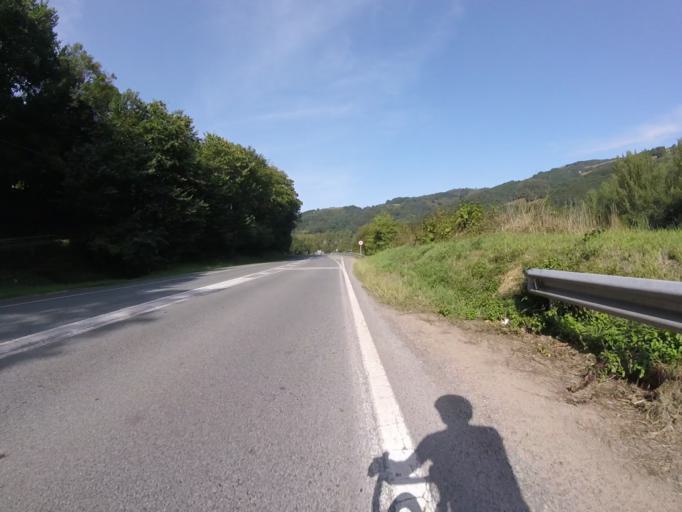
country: ES
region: Navarre
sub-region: Provincia de Navarra
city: Doneztebe
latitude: 43.1405
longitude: -1.5613
